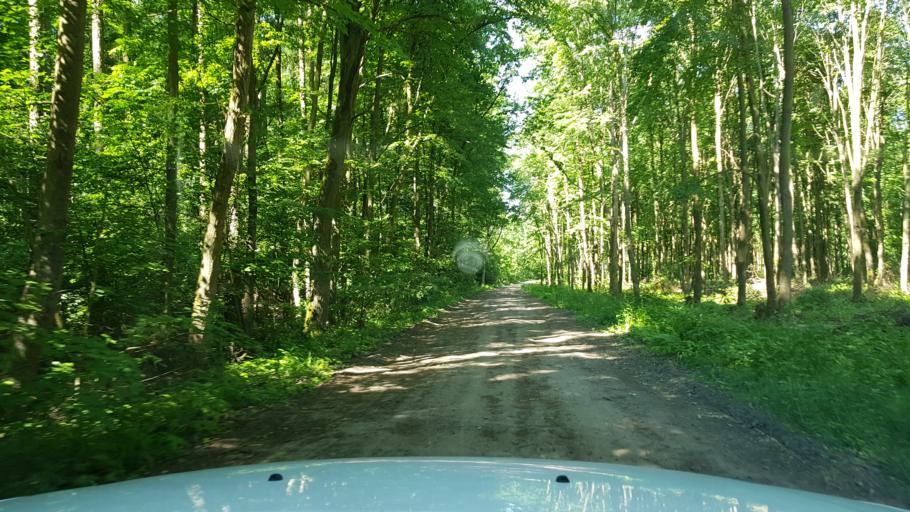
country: PL
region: West Pomeranian Voivodeship
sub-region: Powiat gryfinski
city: Banie
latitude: 53.1195
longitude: 14.5420
